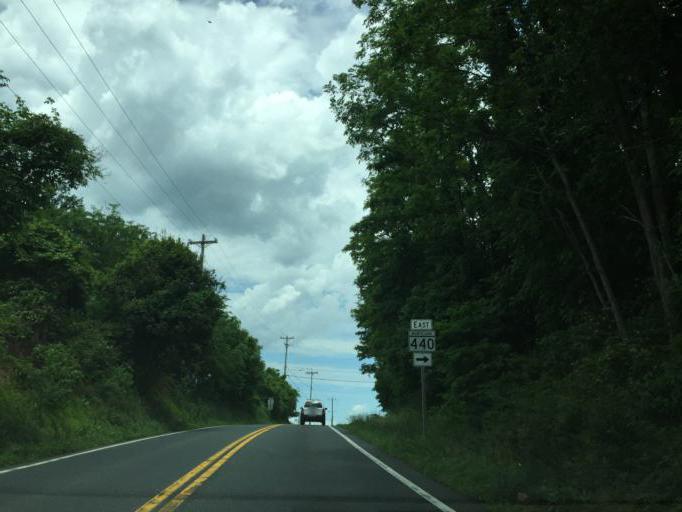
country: US
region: Maryland
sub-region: Harford County
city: Bel Air North
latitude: 39.6378
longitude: -76.3324
